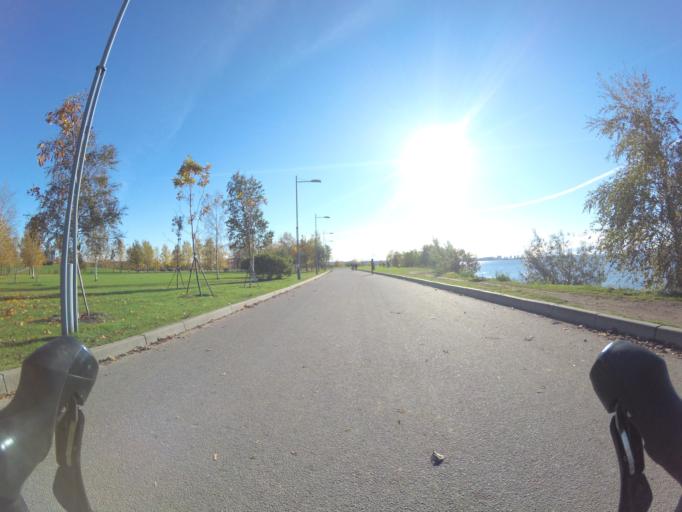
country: RU
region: Leningrad
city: Untolovo
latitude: 59.9842
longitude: 30.1889
